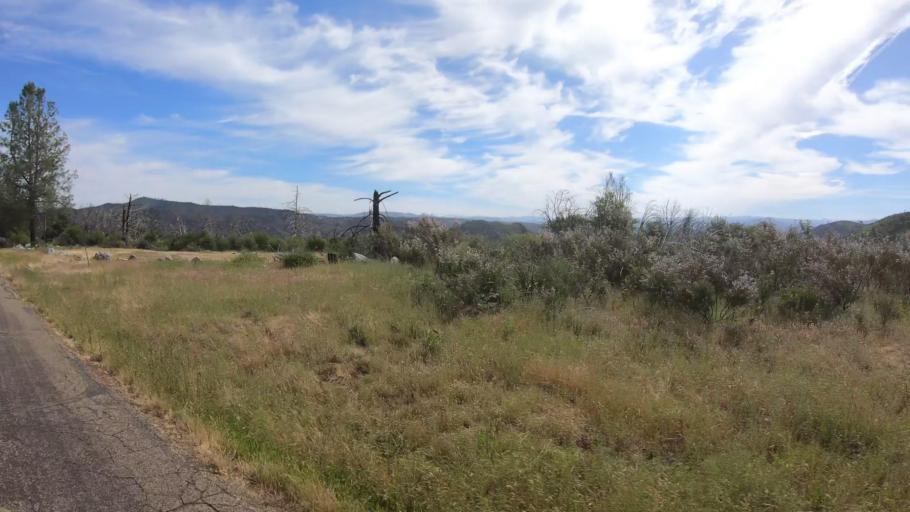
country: US
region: California
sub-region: Tuolumne County
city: Tuolumne City
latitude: 37.8346
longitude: -120.1230
